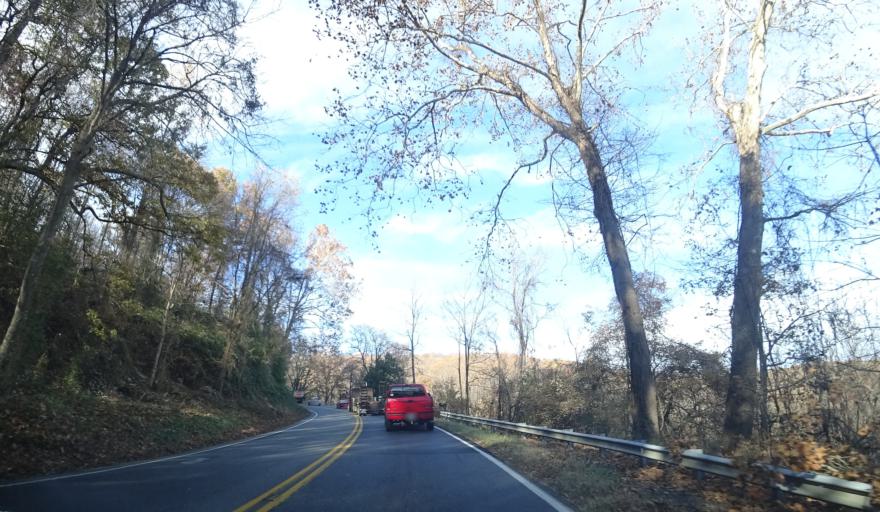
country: US
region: Virginia
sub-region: Greene County
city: Stanardsville
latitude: 38.3232
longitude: -78.4769
